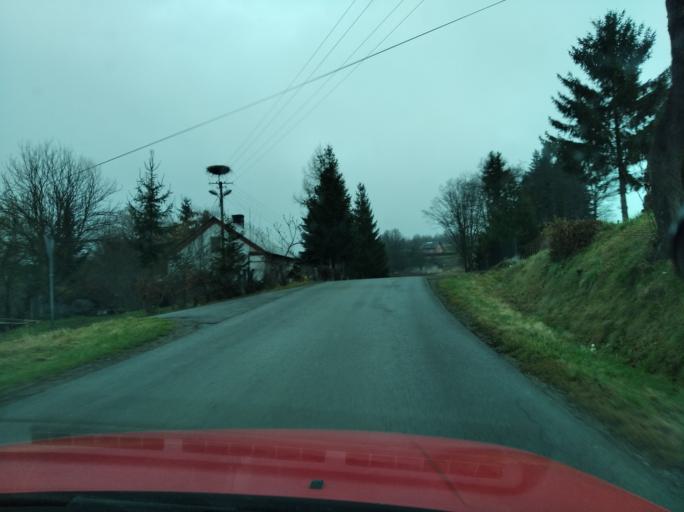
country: PL
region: Subcarpathian Voivodeship
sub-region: Powiat przemyski
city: Nienadowa
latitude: 49.8702
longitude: 22.4192
